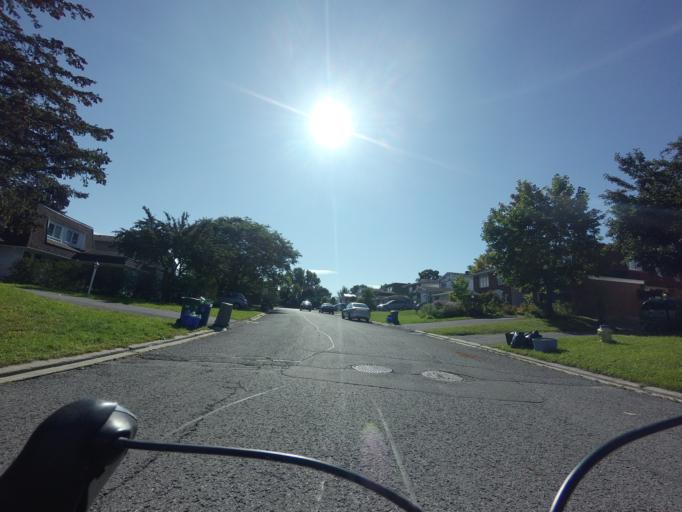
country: CA
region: Ontario
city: Bells Corners
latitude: 45.3164
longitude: -75.8412
